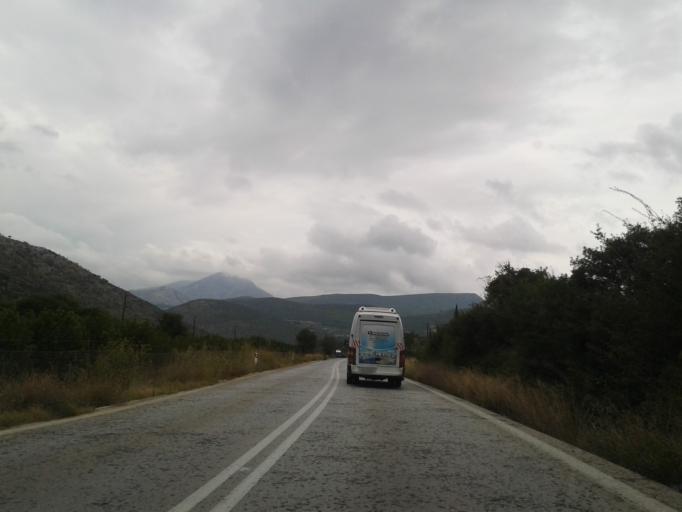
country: GR
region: Peloponnese
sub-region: Nomos Korinthias
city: Ayios Vasilios
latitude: 37.7907
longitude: 22.7425
